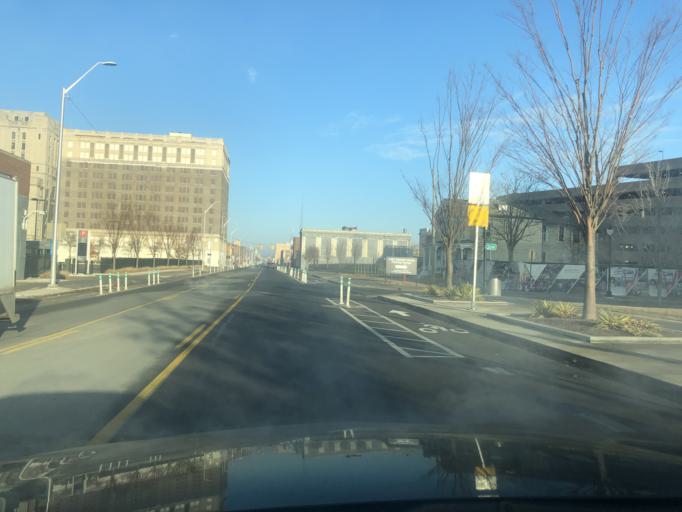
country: US
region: Michigan
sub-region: Wayne County
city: Detroit
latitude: 42.3405
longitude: -83.0578
